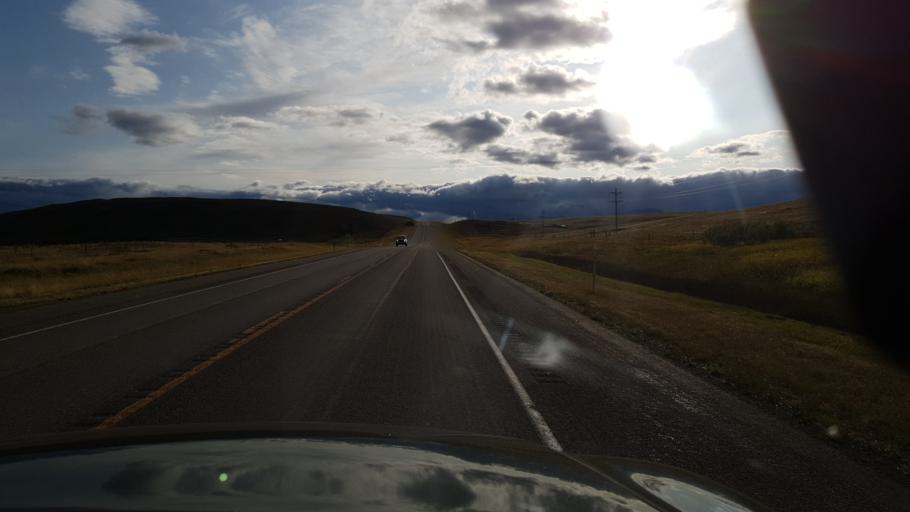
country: US
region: Montana
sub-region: Glacier County
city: South Browning
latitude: 48.5227
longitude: -113.0708
